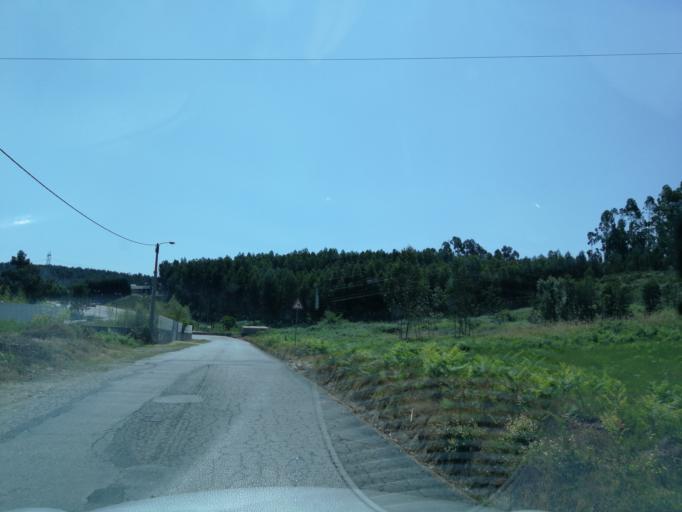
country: PT
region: Braga
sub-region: Povoa de Lanhoso
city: Povoa de Lanhoso
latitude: 41.5813
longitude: -8.3187
